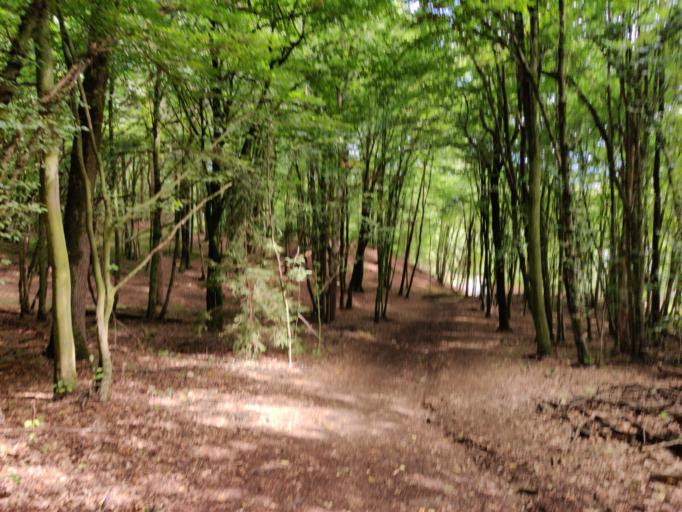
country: AT
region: Carinthia
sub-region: Klagenfurt am Woerthersee
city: Klagenfurt am Woerthersee
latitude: 46.6268
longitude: 14.2661
